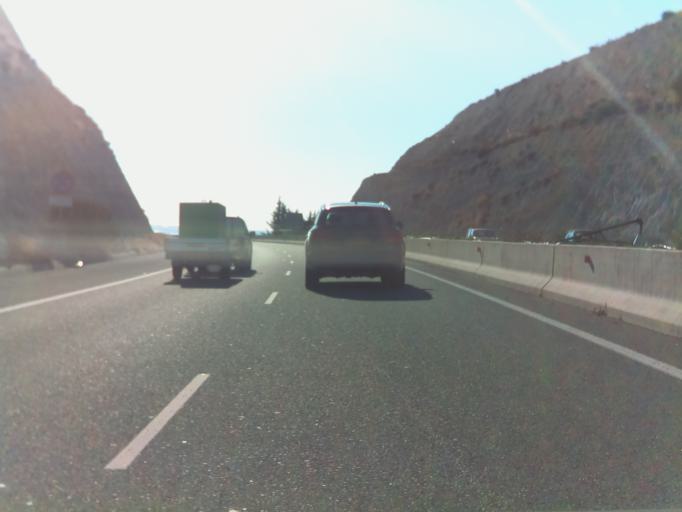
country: CY
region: Limassol
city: Sotira
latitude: 34.6951
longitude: 32.8627
